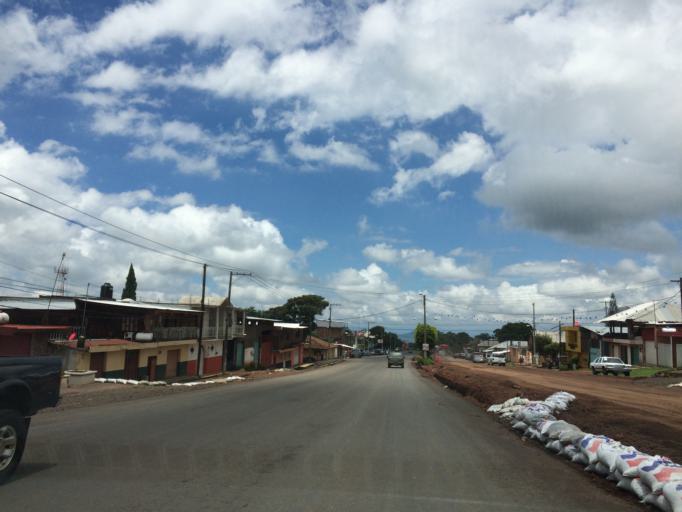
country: MX
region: Michoacan
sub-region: Uruapan
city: Nuevo Zirosto
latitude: 19.5483
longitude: -102.3456
